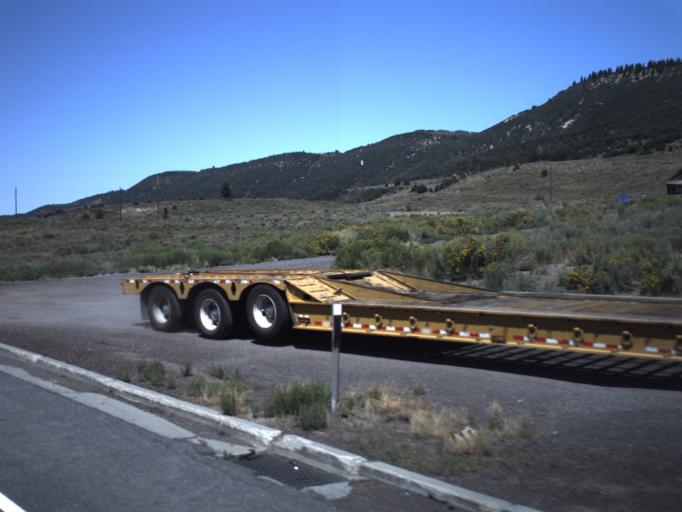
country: US
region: Utah
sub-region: Carbon County
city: Helper
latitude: 39.9286
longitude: -111.0803
